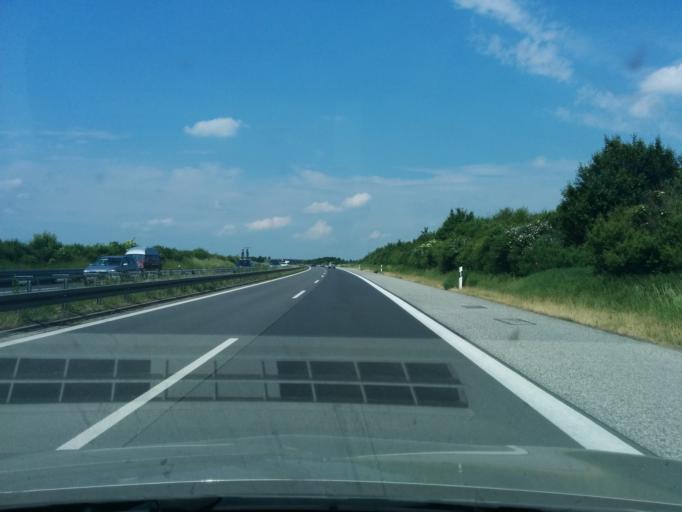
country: DE
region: Brandenburg
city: Gramzow
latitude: 53.2656
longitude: 13.9974
